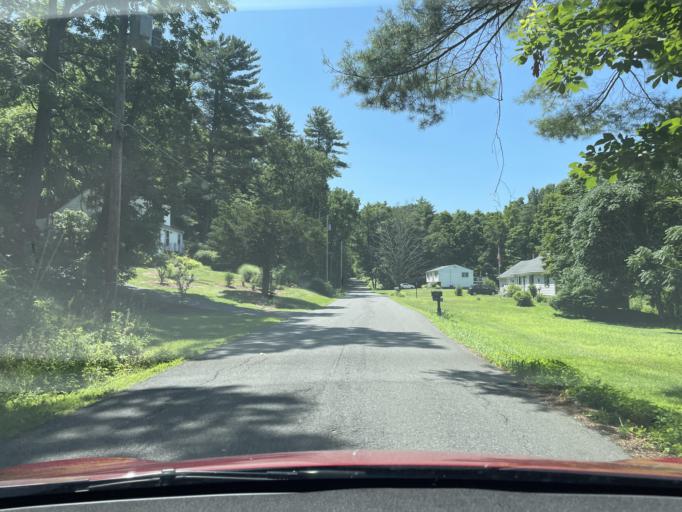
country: US
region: New York
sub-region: Ulster County
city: Glasco
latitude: 42.0263
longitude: -73.9734
